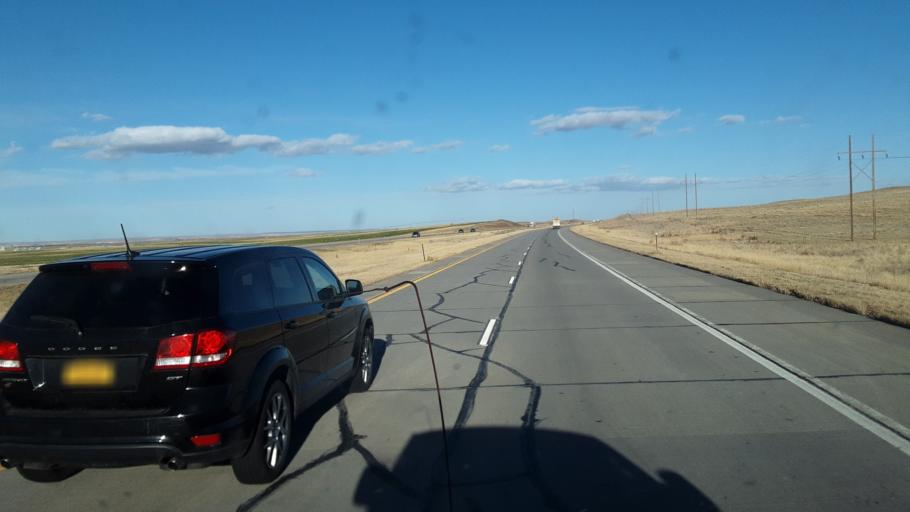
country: US
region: Colorado
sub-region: Logan County
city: Sterling
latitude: 40.7536
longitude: -102.9791
